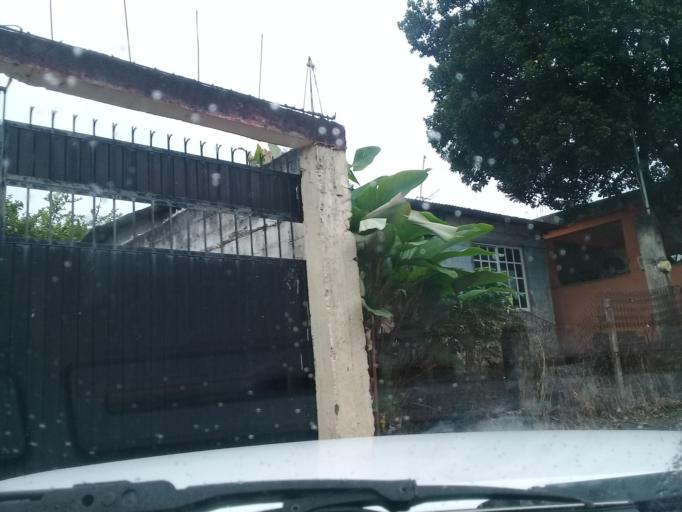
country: MX
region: Veracruz
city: San Andres Tuxtla
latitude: 18.4411
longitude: -95.2074
